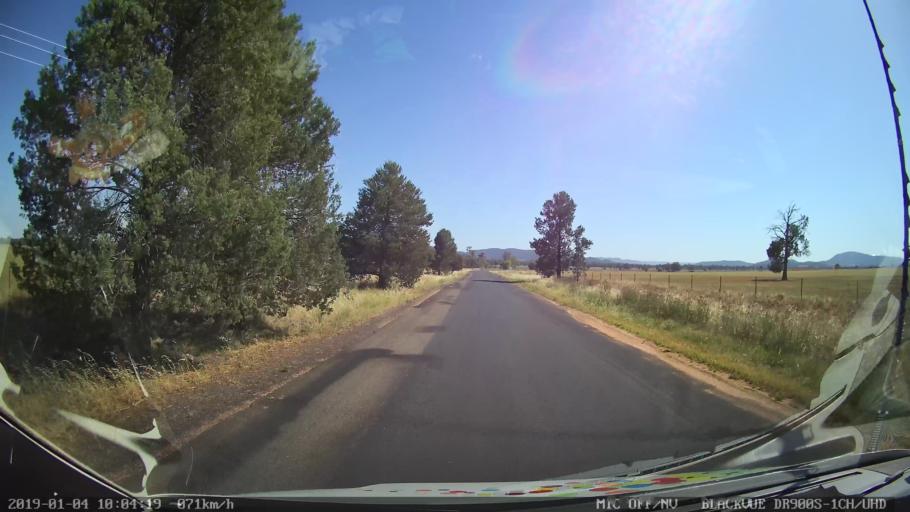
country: AU
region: New South Wales
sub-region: Cabonne
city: Canowindra
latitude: -33.4541
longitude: 148.3607
